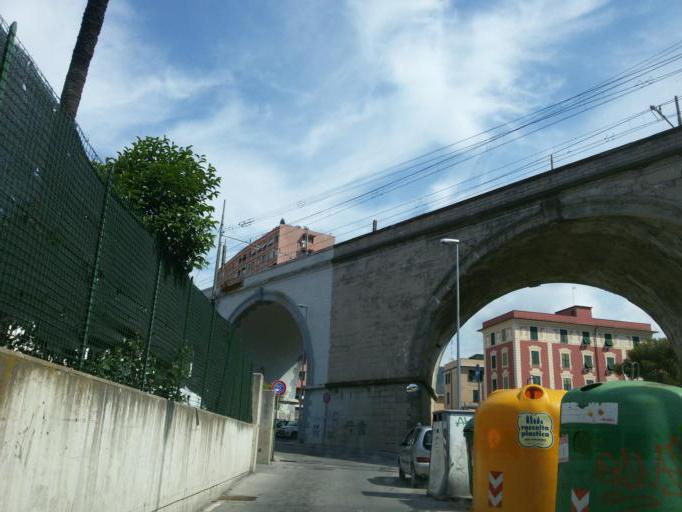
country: IT
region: Liguria
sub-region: Provincia di Genova
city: Genoa
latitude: 44.3946
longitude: 8.9854
